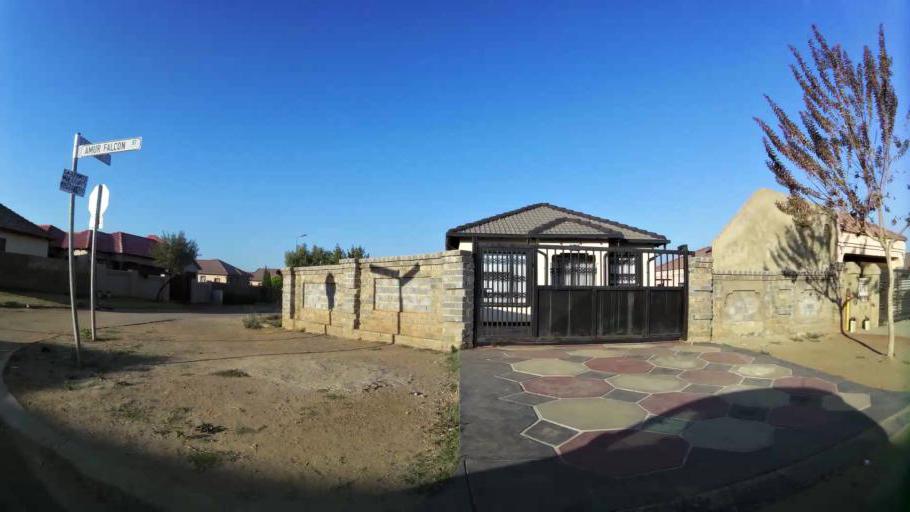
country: ZA
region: Gauteng
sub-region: City of Tshwane Metropolitan Municipality
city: Pretoria
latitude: -25.7402
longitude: 28.1133
